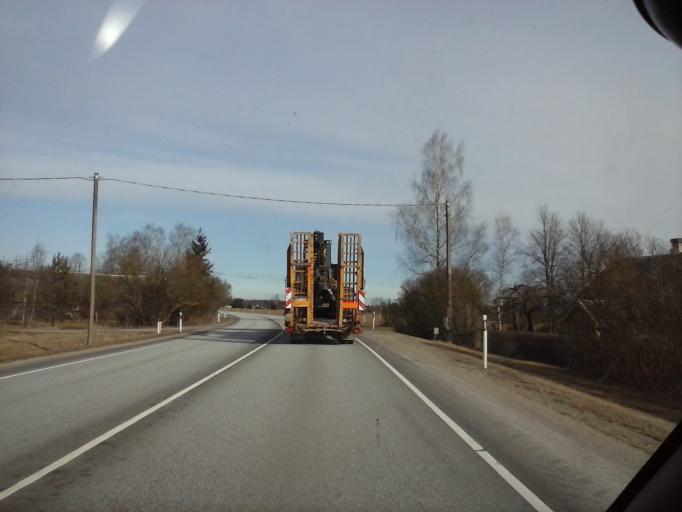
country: EE
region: Jaervamaa
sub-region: Paide linn
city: Paide
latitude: 58.8713
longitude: 25.7024
